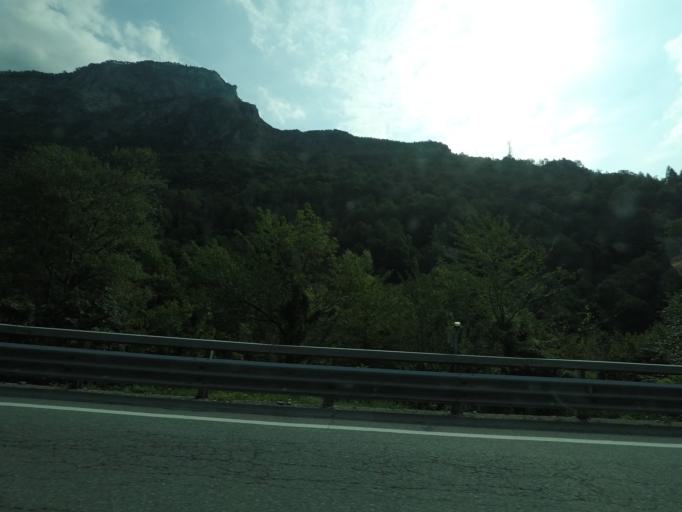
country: IT
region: Aosta Valley
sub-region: Valle d'Aosta
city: Chatillon
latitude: 45.7576
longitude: 7.6081
